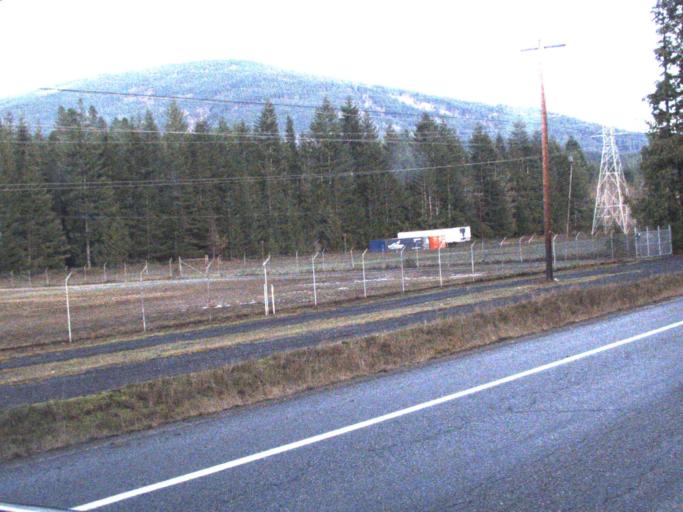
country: US
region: Washington
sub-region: Snohomish County
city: Darrington
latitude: 48.2730
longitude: -121.6551
